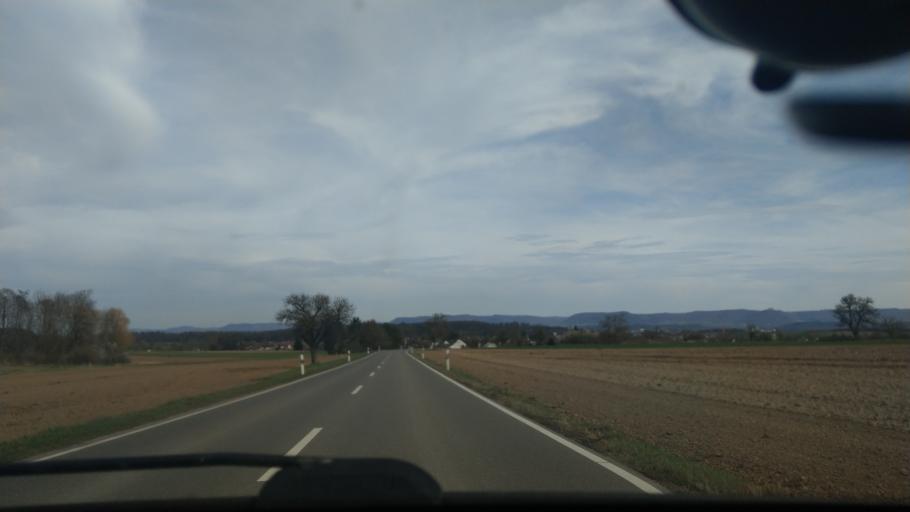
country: DE
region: Baden-Wuerttemberg
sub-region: Regierungsbezirk Stuttgart
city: Wolfschlugen
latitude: 48.6621
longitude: 9.2764
